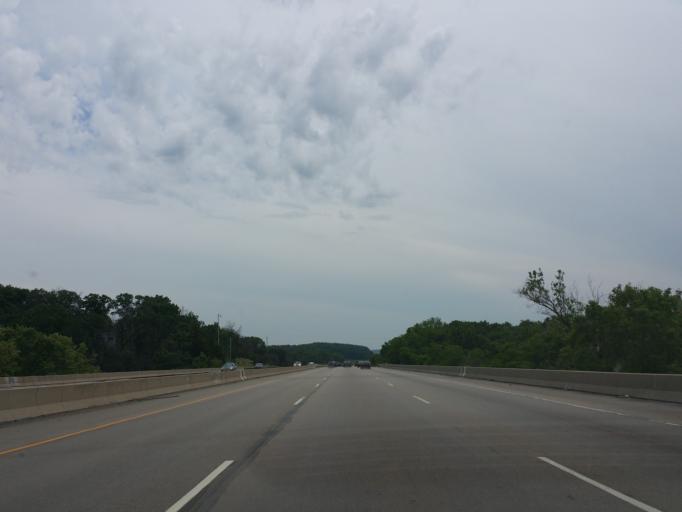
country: US
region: Wisconsin
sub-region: Columbia County
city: Portage
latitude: 43.4468
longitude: -89.4933
